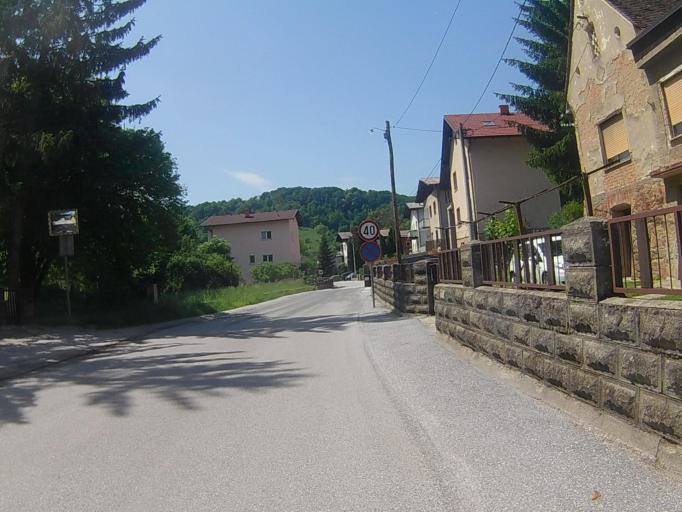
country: SI
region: Maribor
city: Maribor
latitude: 46.5749
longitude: 15.6634
